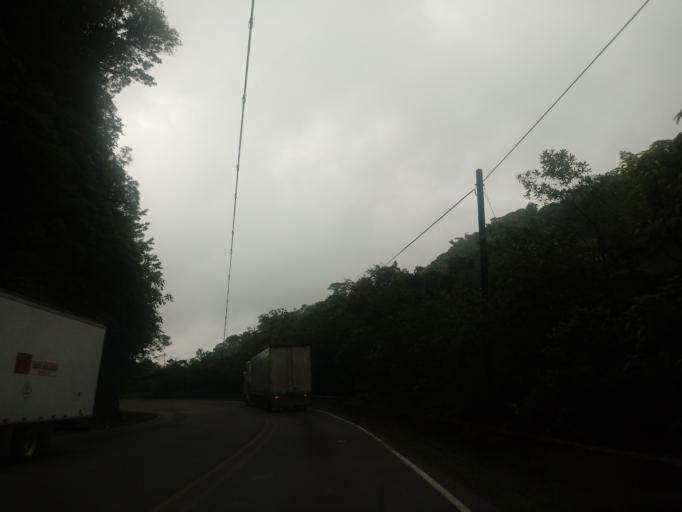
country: CR
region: Heredia
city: Angeles
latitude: 10.0575
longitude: -84.0112
